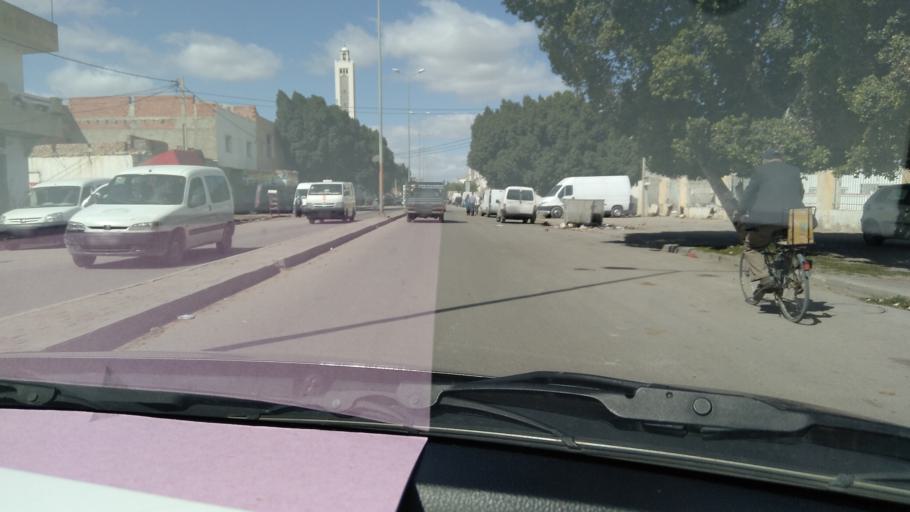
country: TN
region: Al Qayrawan
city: Kairouan
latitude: 35.6807
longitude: 10.0844
